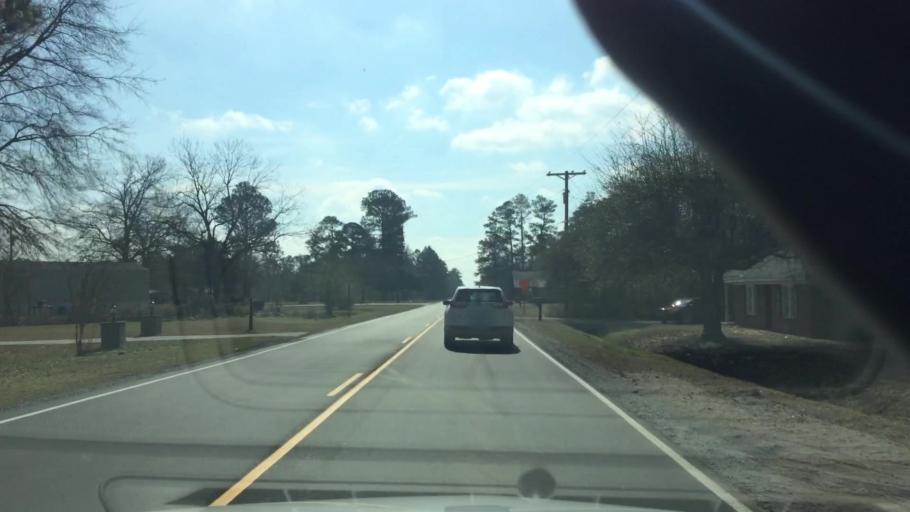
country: US
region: North Carolina
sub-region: Duplin County
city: Beulaville
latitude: 34.9810
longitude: -77.7598
